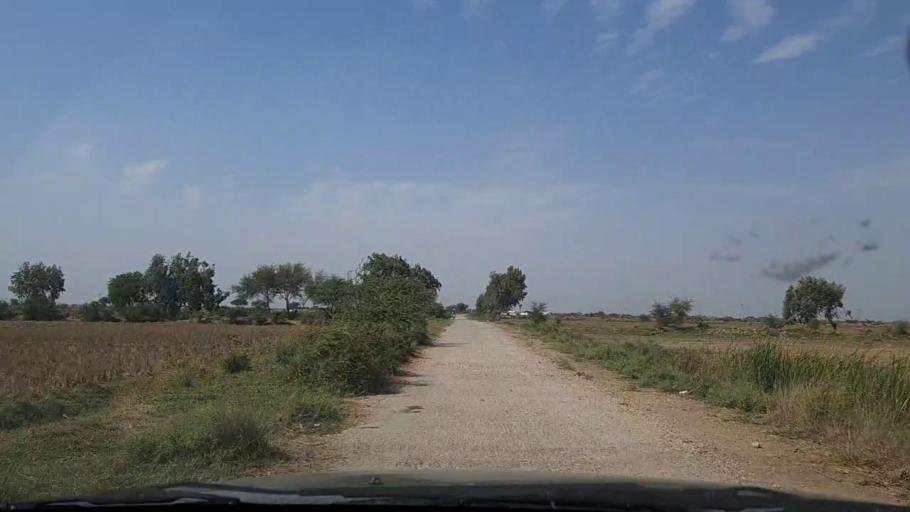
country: PK
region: Sindh
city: Mirpur Batoro
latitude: 24.5926
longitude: 68.2082
